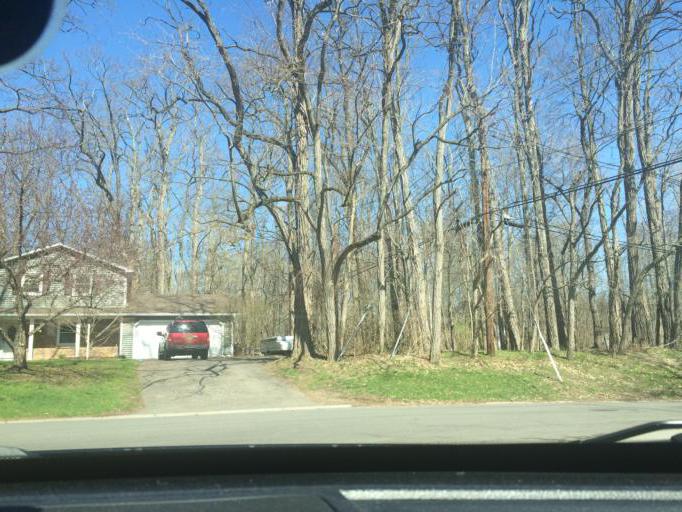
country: US
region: New York
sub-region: Monroe County
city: East Rochester
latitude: 43.0945
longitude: -77.4720
